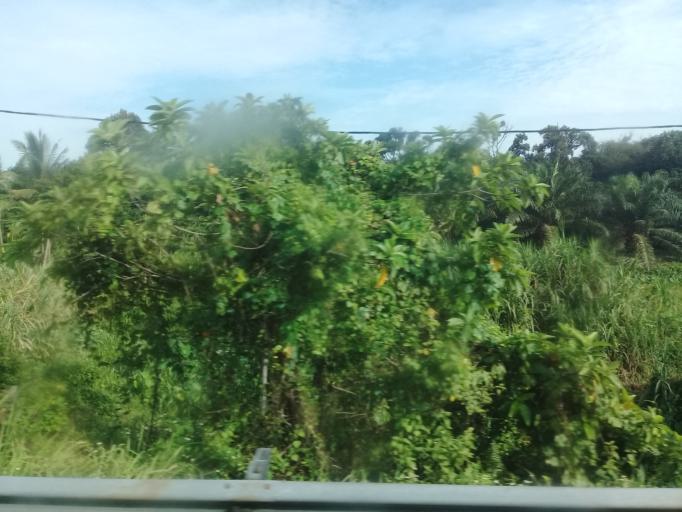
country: MY
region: Perak
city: Batu Gajah
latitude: 4.4789
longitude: 101.0008
